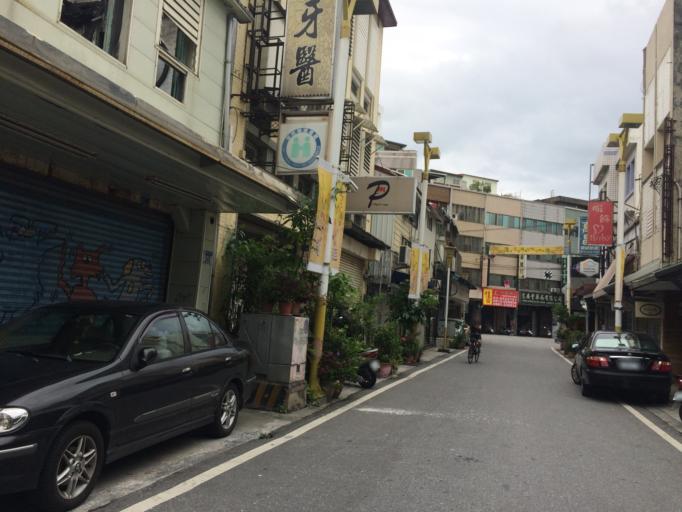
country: TW
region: Taiwan
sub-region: Hualien
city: Hualian
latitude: 23.9757
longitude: 121.6079
